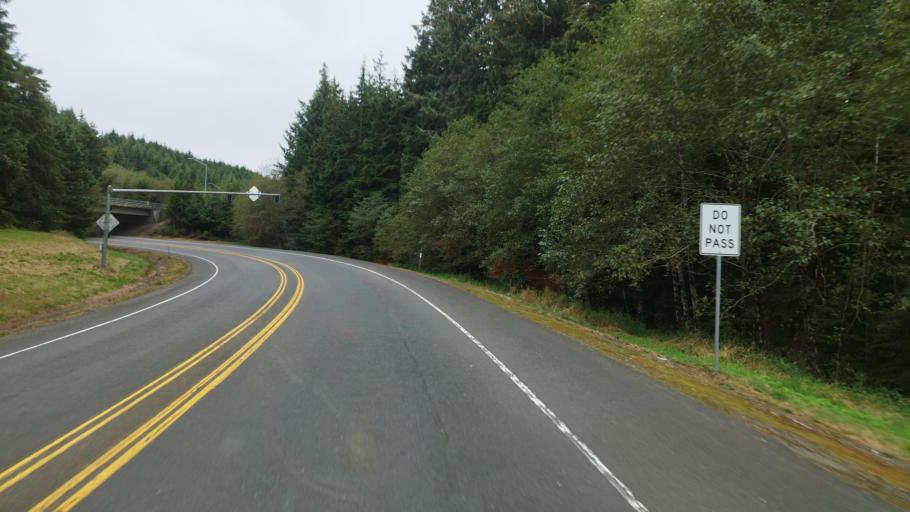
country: US
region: Oregon
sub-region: Clatsop County
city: Seaside
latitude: 45.9395
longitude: -123.9208
